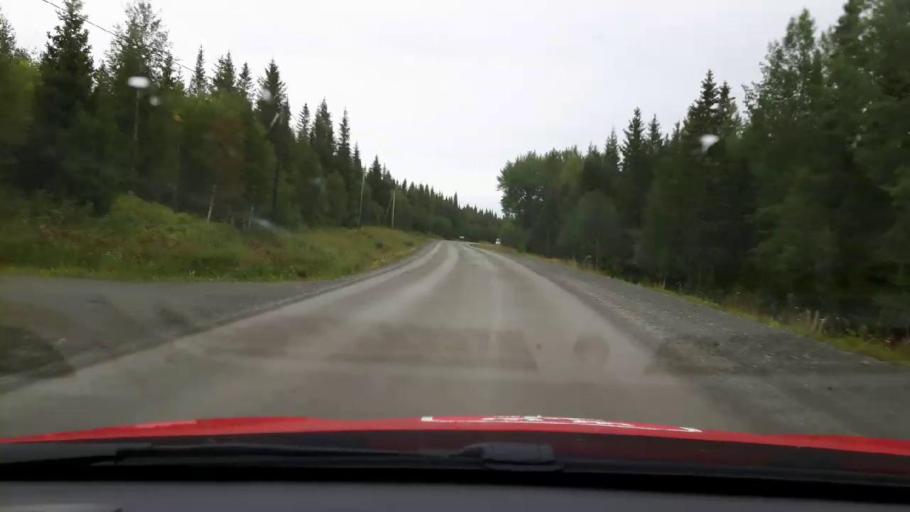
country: SE
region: Jaemtland
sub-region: Are Kommun
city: Are
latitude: 63.4543
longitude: 12.6470
